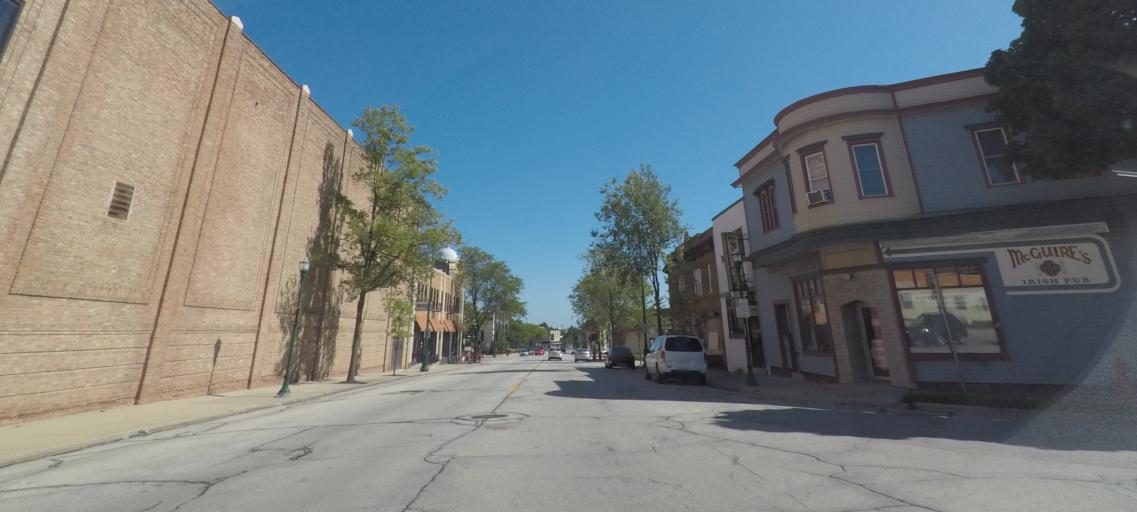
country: US
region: Wisconsin
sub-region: Milwaukee County
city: West Allis
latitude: 43.0162
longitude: -87.9912
